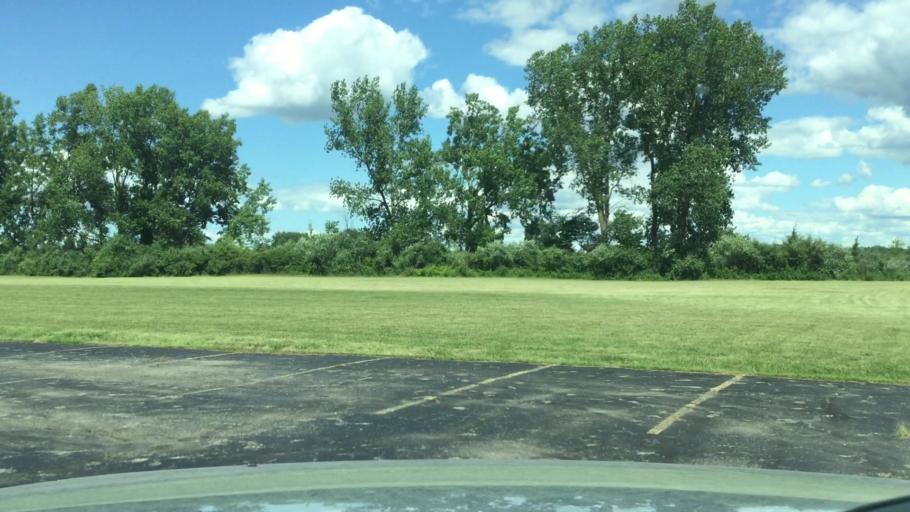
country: US
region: Michigan
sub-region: Saginaw County
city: Shields
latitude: 43.3801
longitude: -84.1172
